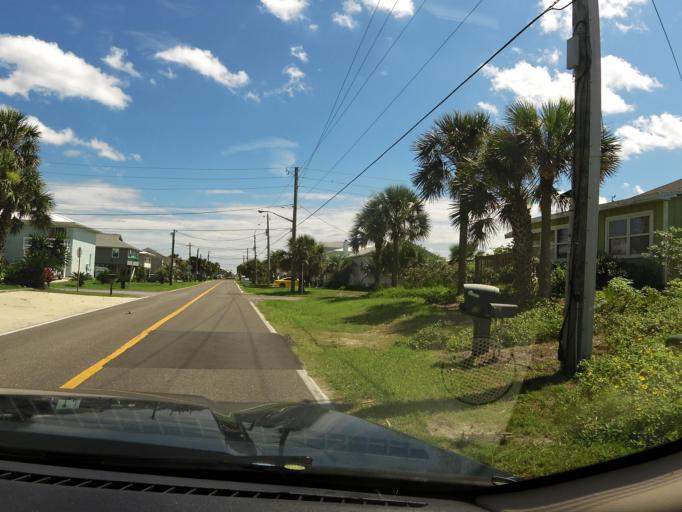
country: US
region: Florida
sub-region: Nassau County
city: Fernandina Beach
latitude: 30.6720
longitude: -81.4310
